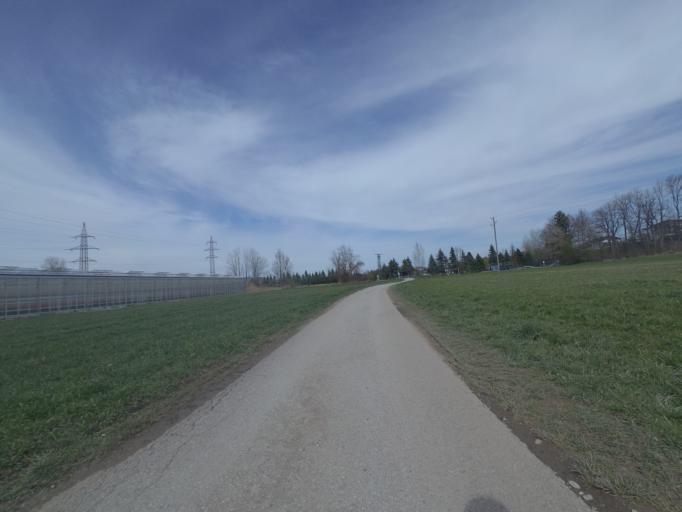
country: DE
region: Bavaria
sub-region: Upper Bavaria
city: Ainring
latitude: 47.8052
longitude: 12.9784
